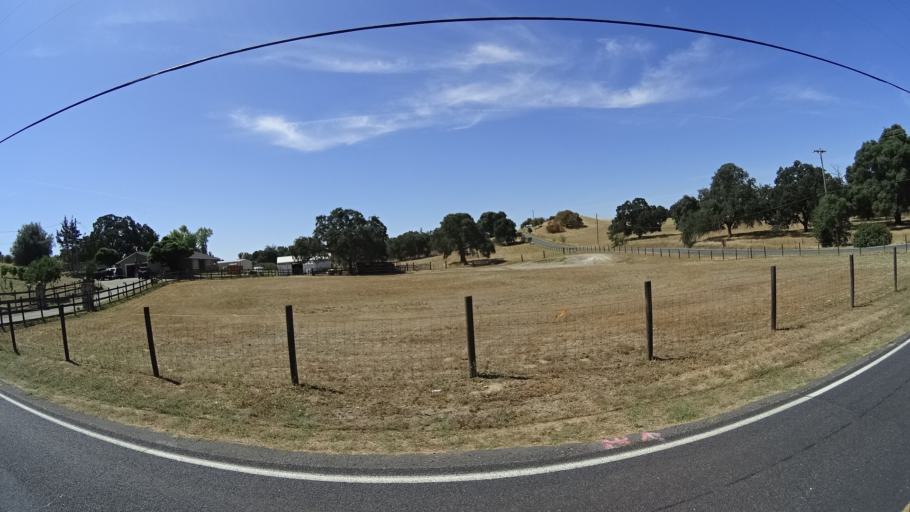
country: US
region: California
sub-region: Calaveras County
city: Rancho Calaveras
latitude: 38.1486
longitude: -120.9444
